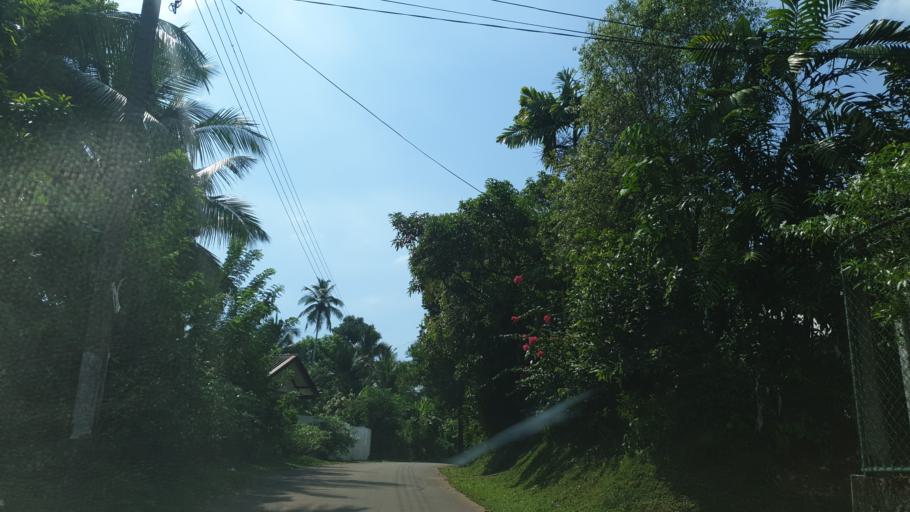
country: LK
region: Western
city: Panadura
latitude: 6.7238
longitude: 79.9647
